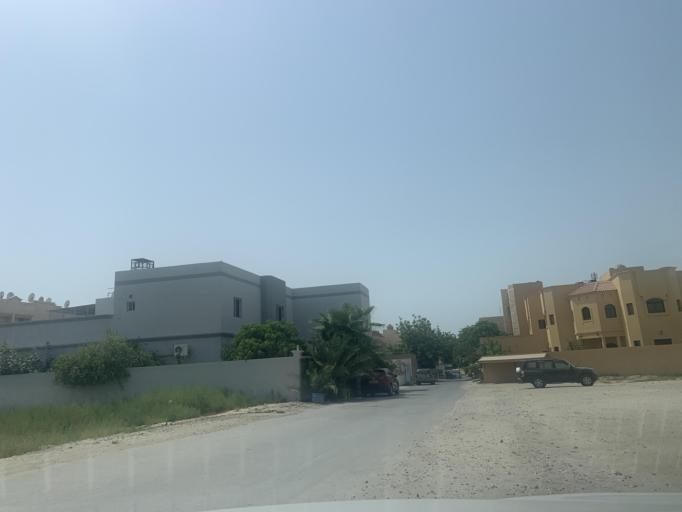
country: BH
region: Manama
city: Jidd Hafs
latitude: 26.2211
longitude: 50.4651
